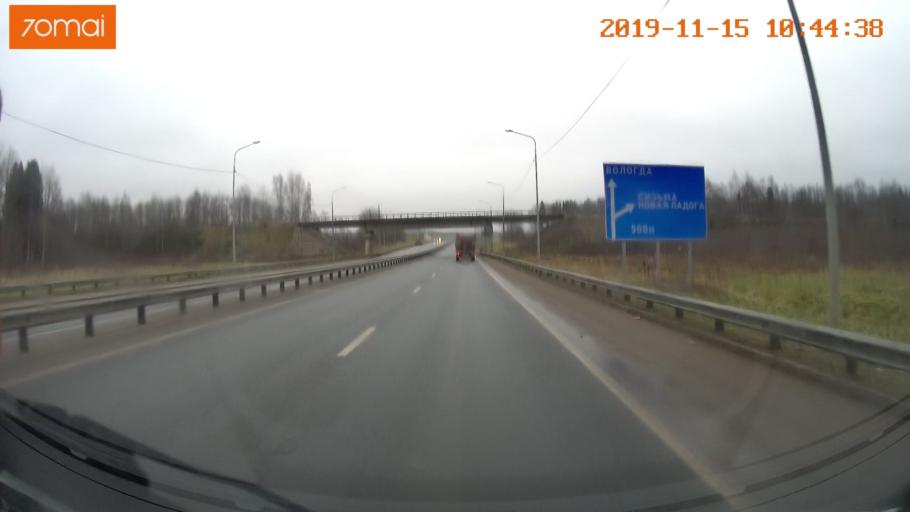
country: RU
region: Vologda
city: Sheksna
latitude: 59.2115
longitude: 38.5633
